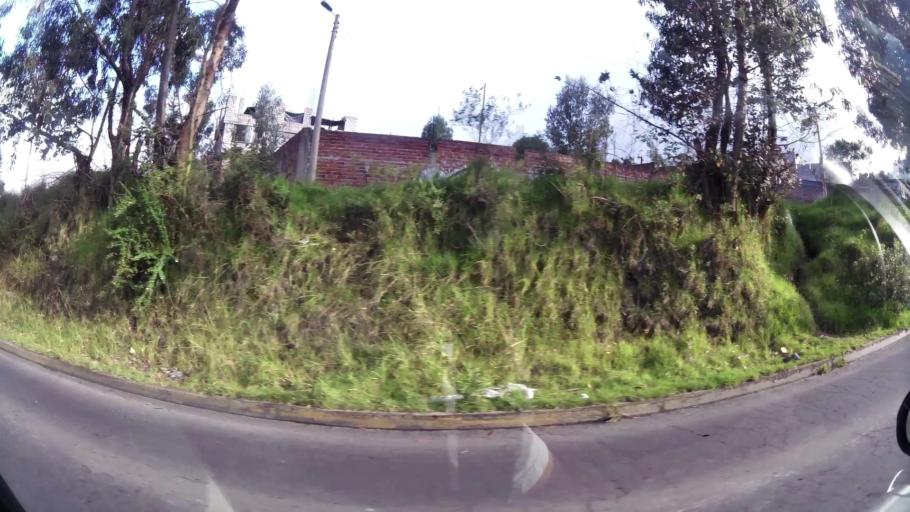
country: EC
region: Pichincha
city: Quito
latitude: -0.2563
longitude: -78.4950
